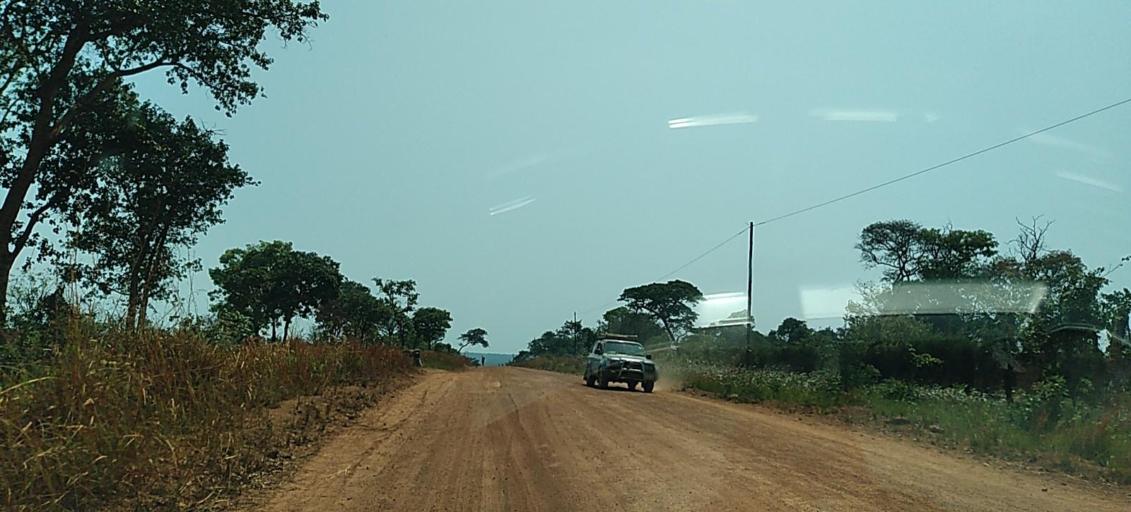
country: ZM
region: North-Western
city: Kansanshi
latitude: -12.0050
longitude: 26.5826
